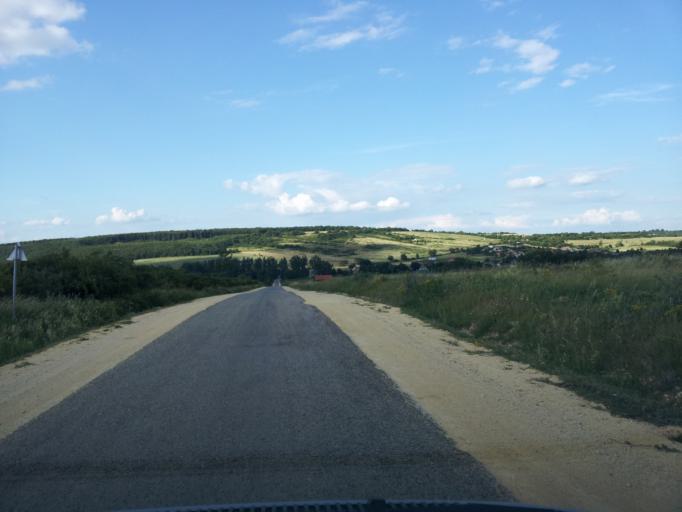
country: HU
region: Veszprem
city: Zirc
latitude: 47.1997
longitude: 17.8417
